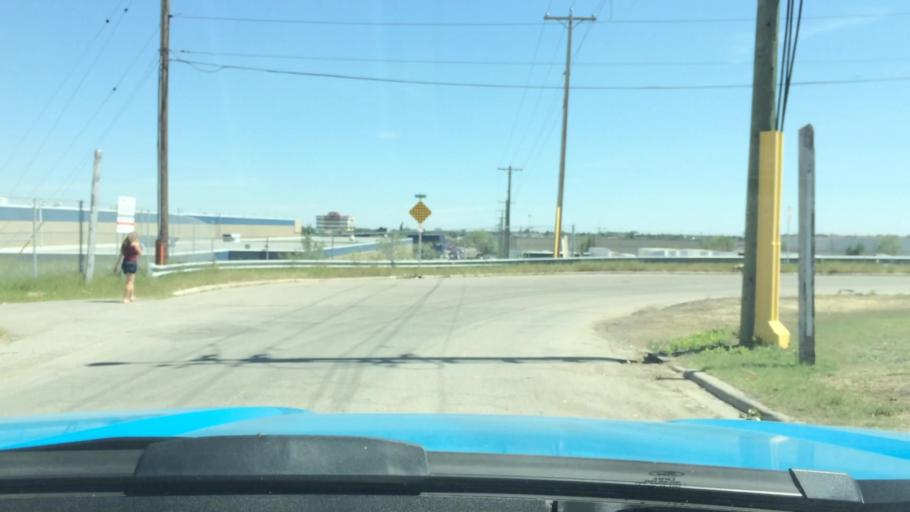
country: CA
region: Alberta
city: Calgary
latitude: 51.0545
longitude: -113.9900
